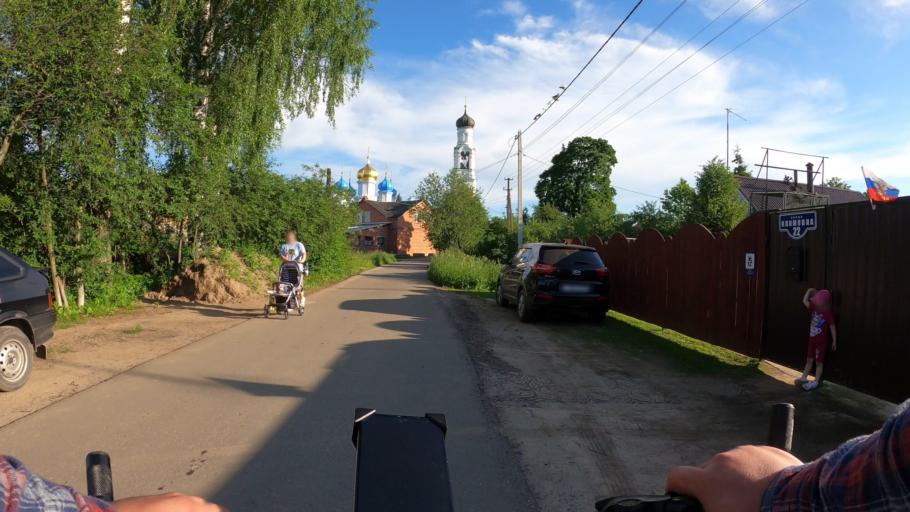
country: RU
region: Moskovskaya
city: Ashitkovo
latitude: 55.4402
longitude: 38.6052
